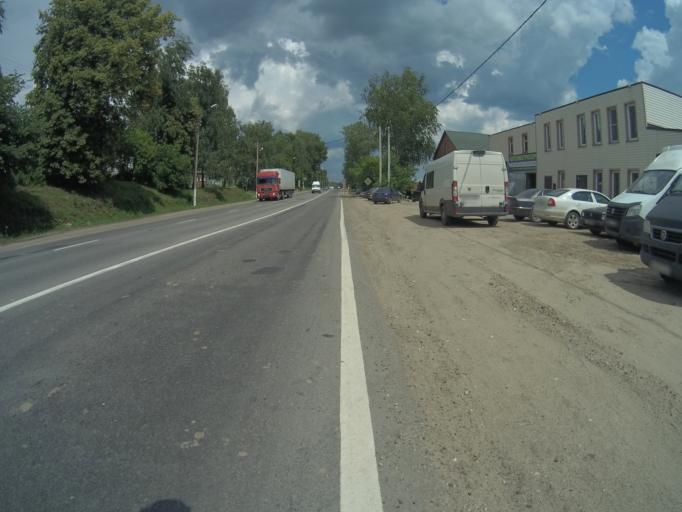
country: RU
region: Vladimir
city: Bogolyubovo
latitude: 56.1903
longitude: 40.5244
